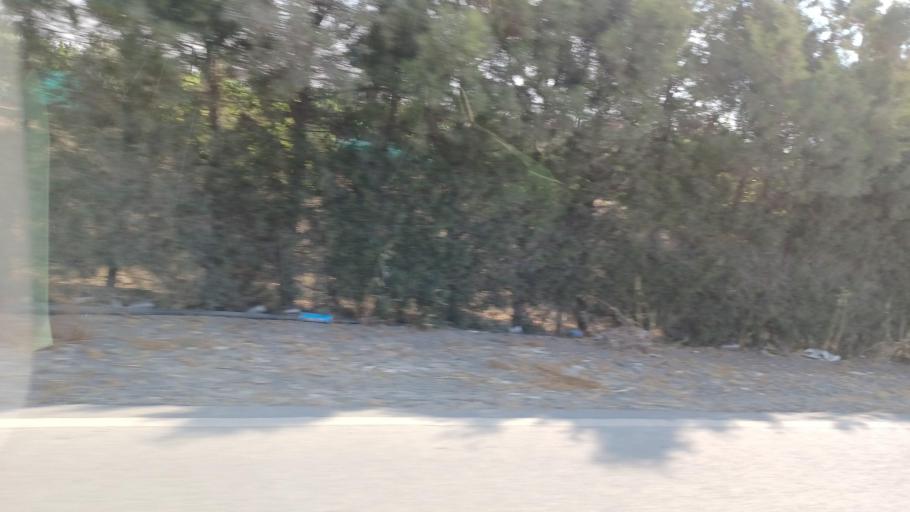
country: CY
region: Larnaka
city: Dhromolaxia
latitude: 34.8766
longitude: 33.5803
